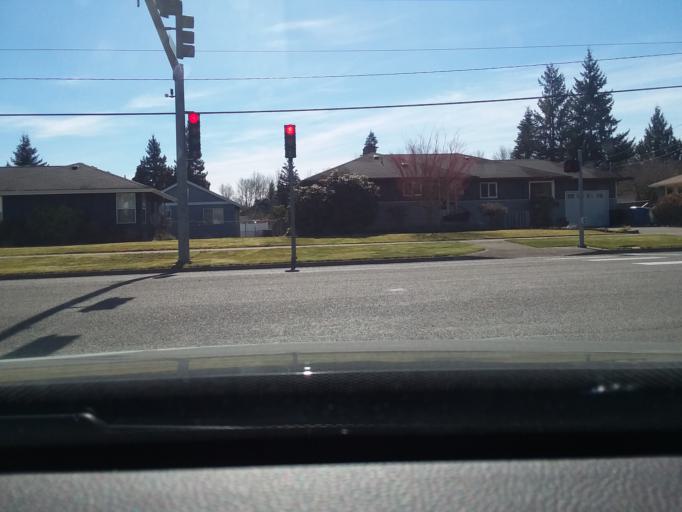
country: US
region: Washington
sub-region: Pierce County
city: Sumner
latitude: 47.1991
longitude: -122.2450
